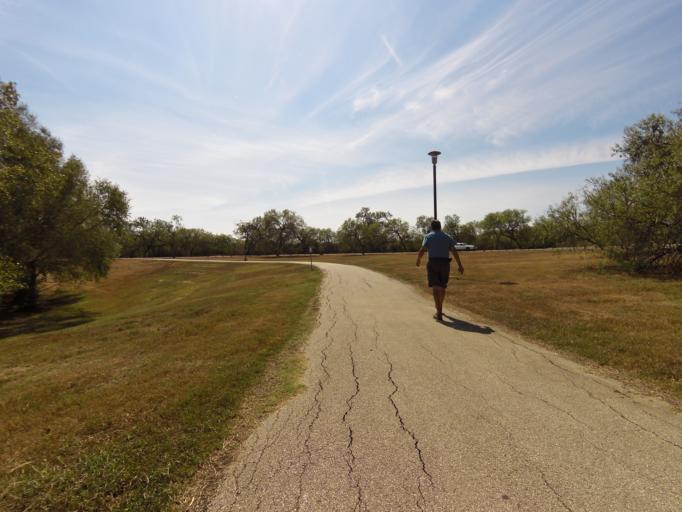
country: US
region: Texas
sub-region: Bexar County
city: San Antonio
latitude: 29.3850
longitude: -98.4298
